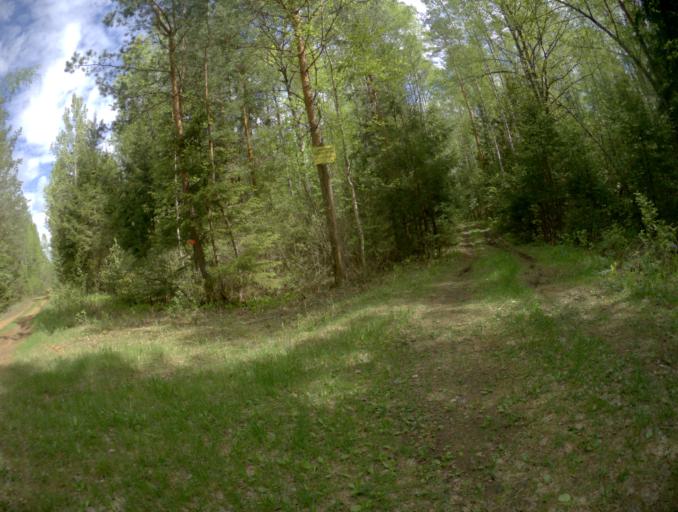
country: RU
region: Moskovskaya
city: Cherusti
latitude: 55.4495
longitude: 40.0367
